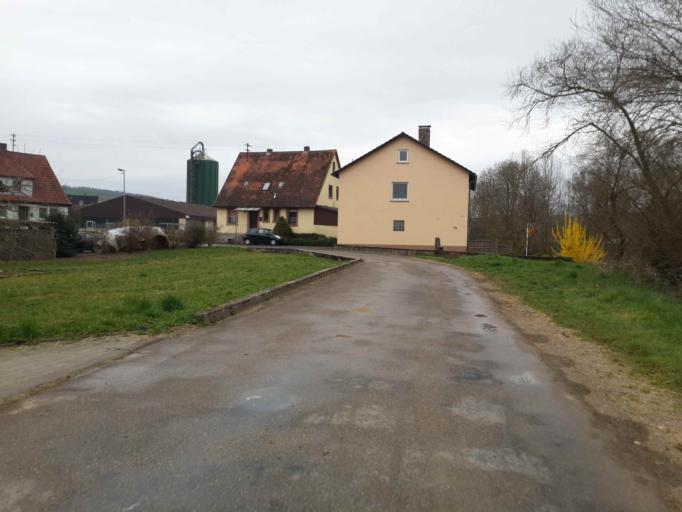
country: DE
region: Baden-Wuerttemberg
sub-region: Regierungsbezirk Stuttgart
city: Bad Mergentheim
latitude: 49.5159
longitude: 9.7464
